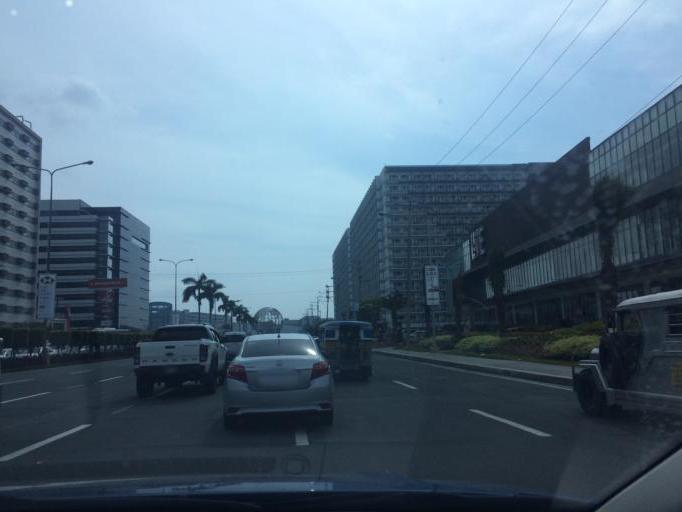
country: PH
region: Metro Manila
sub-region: Makati City
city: Makati City
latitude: 14.5364
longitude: 120.9888
